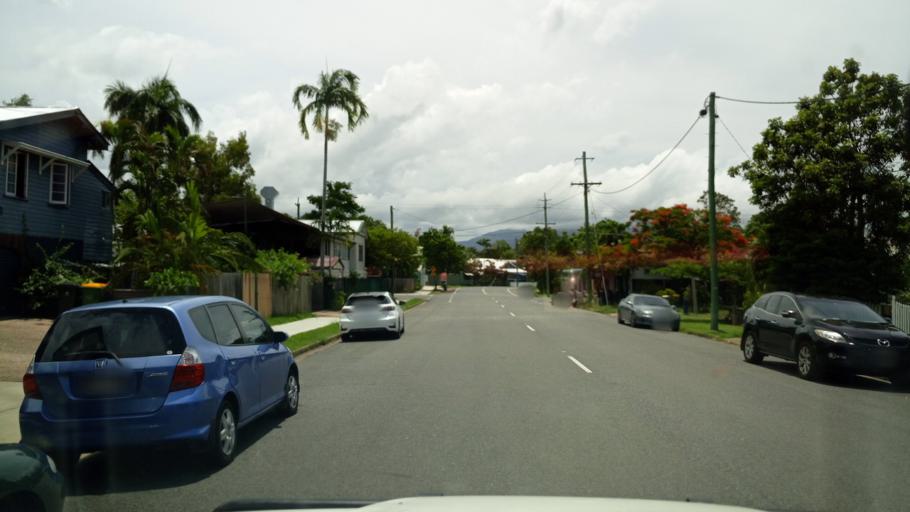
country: AU
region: Queensland
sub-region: Cairns
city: Yorkeys Knob
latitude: -16.8514
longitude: 145.7497
